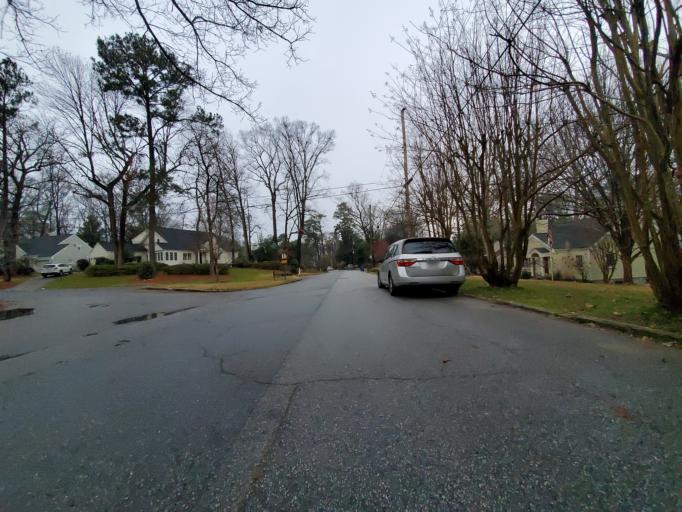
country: US
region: Georgia
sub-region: DeKalb County
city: North Decatur
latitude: 33.7918
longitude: -84.3084
